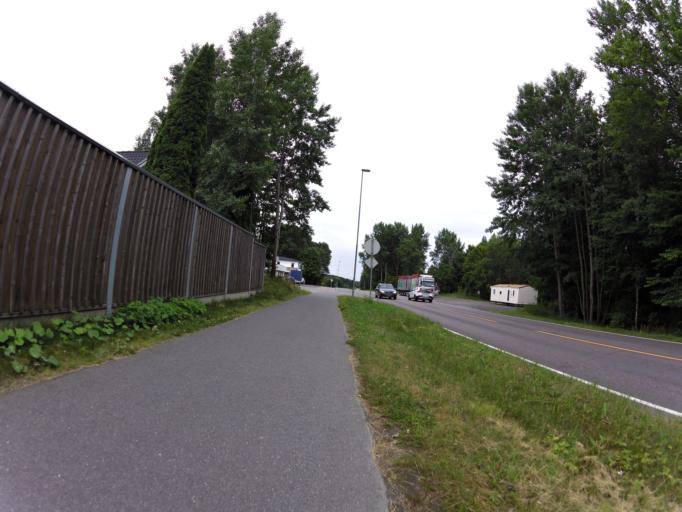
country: NO
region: Akershus
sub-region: Vestby
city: Vestby
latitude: 59.6134
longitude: 10.7401
